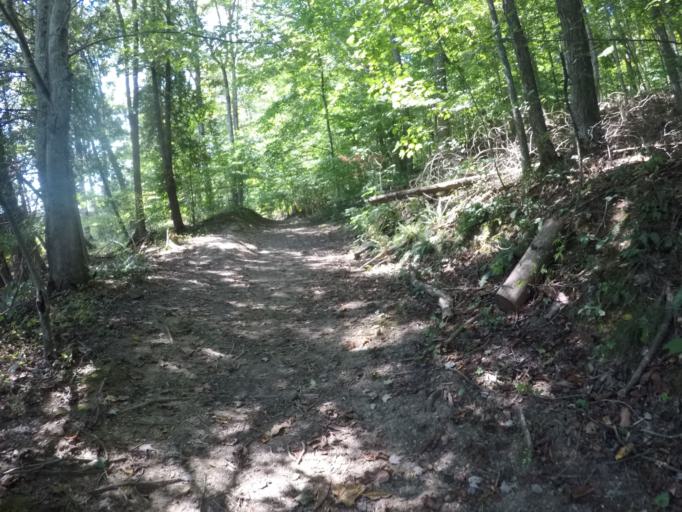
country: US
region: Ohio
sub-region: Lawrence County
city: Ironton
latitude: 38.6160
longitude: -82.6292
